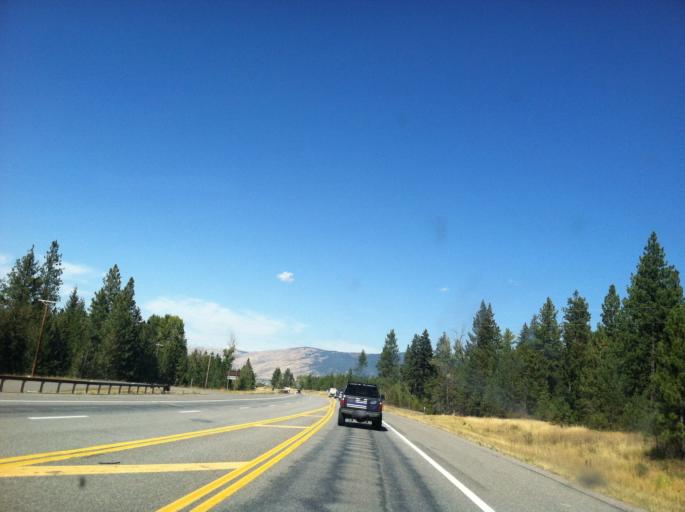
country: US
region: Montana
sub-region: Missoula County
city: Frenchtown
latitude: 47.0912
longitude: -114.0404
